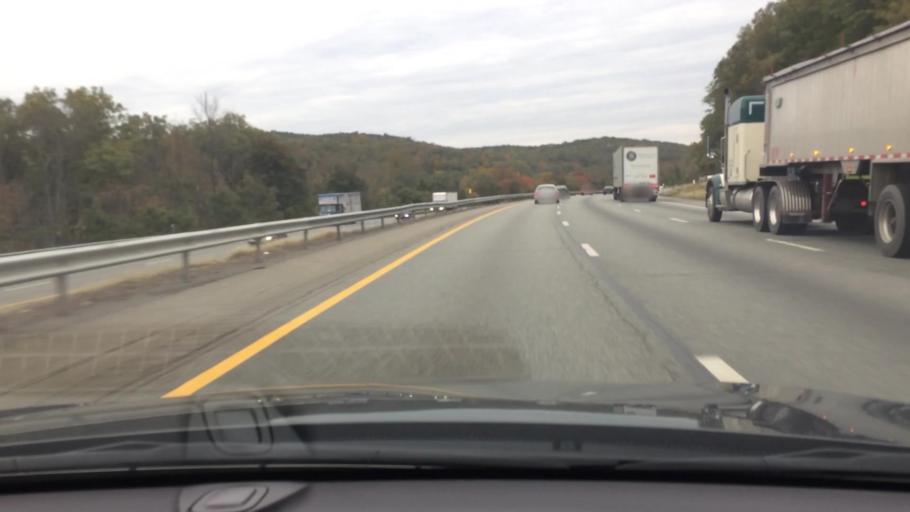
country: US
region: New York
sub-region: Rockland County
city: Sloatsburg
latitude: 41.1705
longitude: -74.1864
